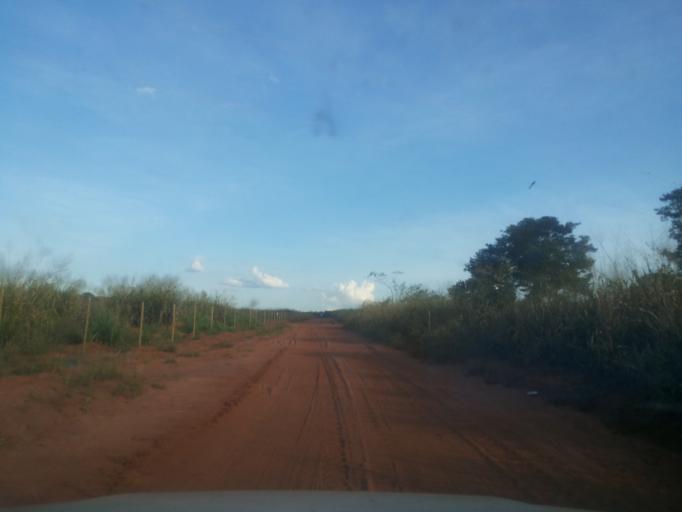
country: BR
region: Minas Gerais
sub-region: Santa Vitoria
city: Santa Vitoria
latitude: -18.9939
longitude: -50.3748
